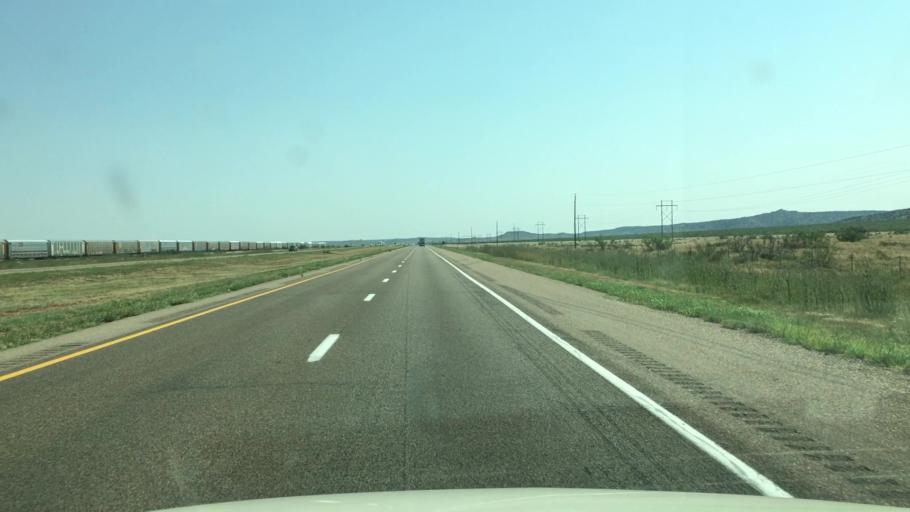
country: US
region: New Mexico
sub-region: Quay County
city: Tucumcari
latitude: 35.1077
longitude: -104.0191
